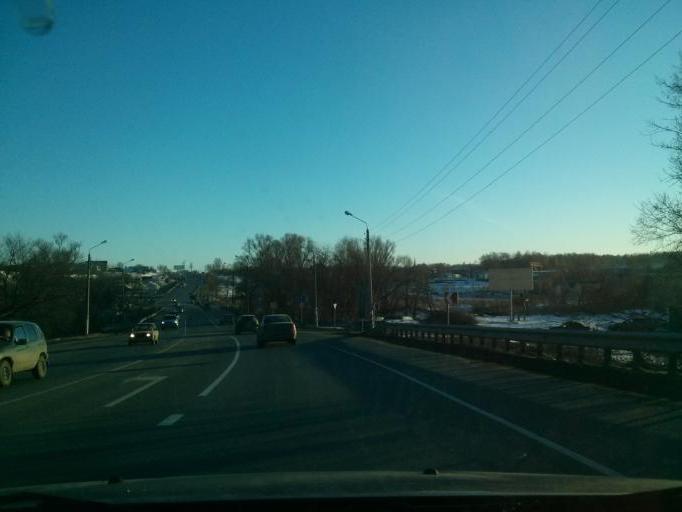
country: RU
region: Nizjnij Novgorod
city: Afonino
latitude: 56.2383
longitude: 44.0992
